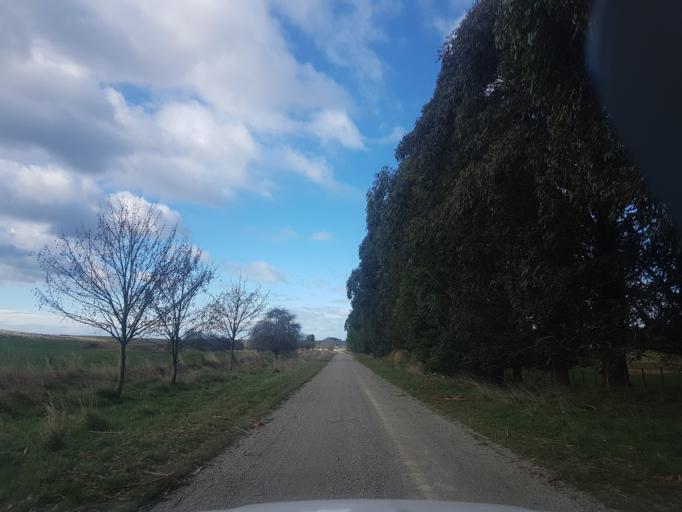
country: NZ
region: Canterbury
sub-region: Timaru District
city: Pleasant Point
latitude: -44.1882
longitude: 171.1702
